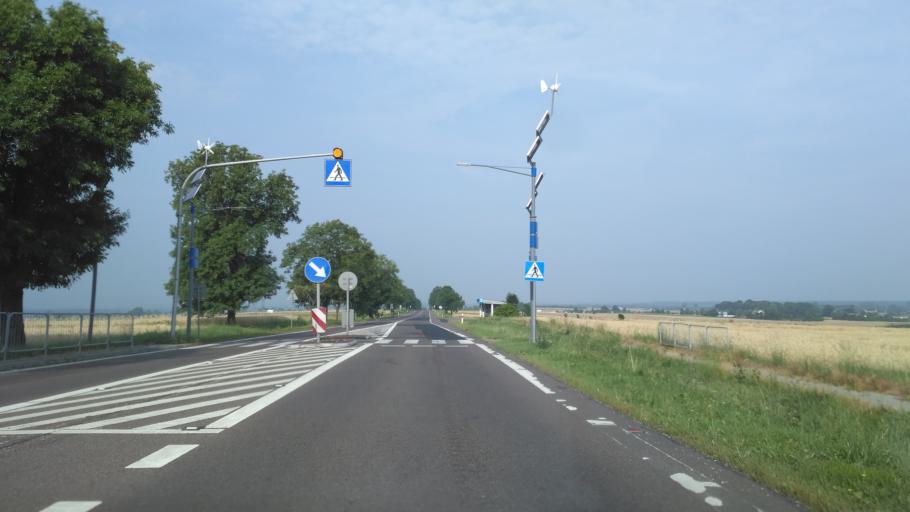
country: PL
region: Lublin Voivodeship
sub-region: Powiat swidnicki
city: Trawniki
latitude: 51.1701
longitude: 23.1084
